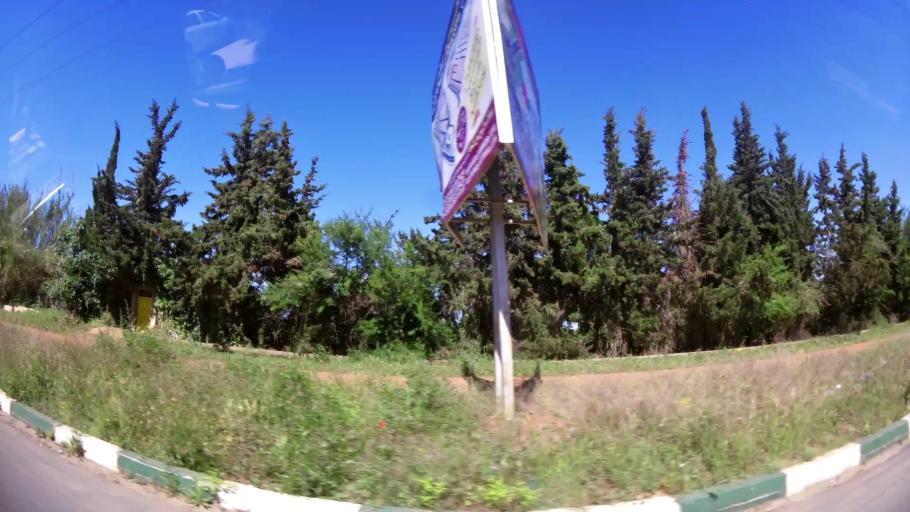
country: MA
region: Oriental
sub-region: Berkane-Taourirt
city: Berkane
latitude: 34.9426
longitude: -2.3256
